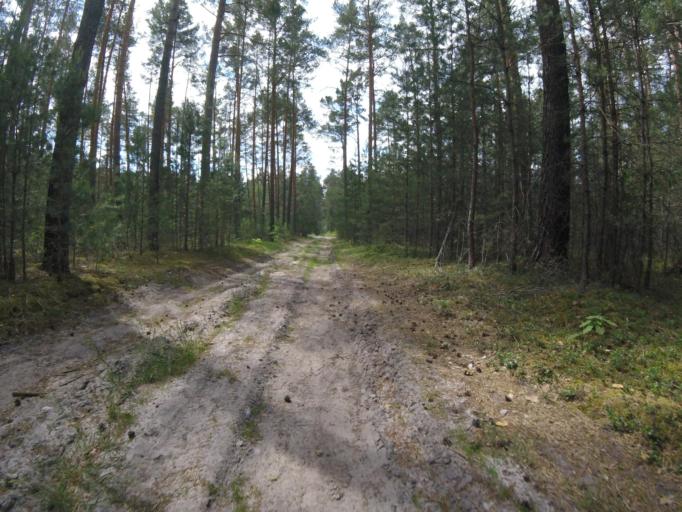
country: DE
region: Brandenburg
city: Halbe
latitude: 52.1111
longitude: 13.6644
